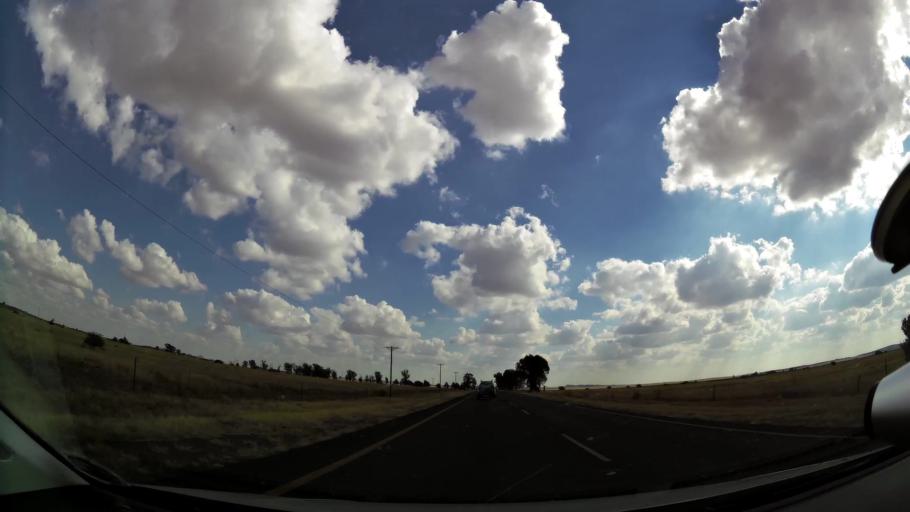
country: ZA
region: Orange Free State
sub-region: Xhariep District Municipality
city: Koffiefontein
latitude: -29.1316
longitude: 25.5318
